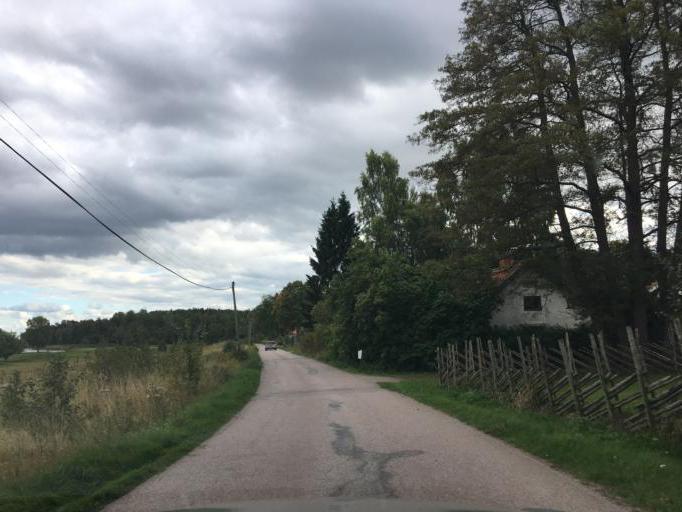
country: SE
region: Vaestmanland
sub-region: Vasteras
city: Tillberga
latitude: 59.5368
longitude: 16.7519
